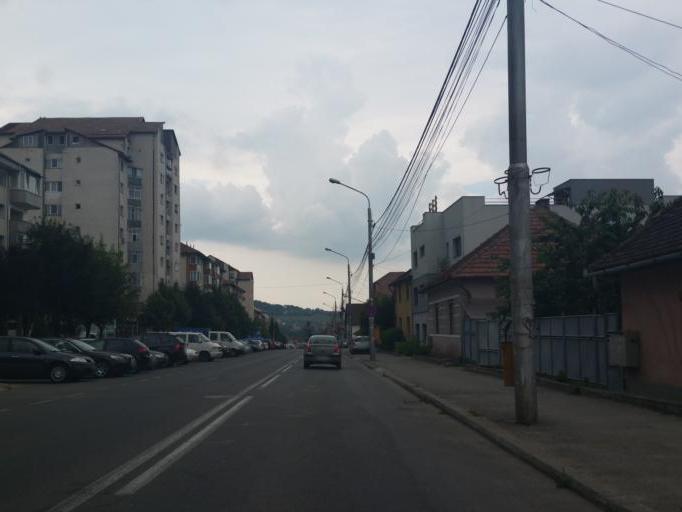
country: RO
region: Salaj
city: Zalau
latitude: 47.1732
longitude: 23.0631
